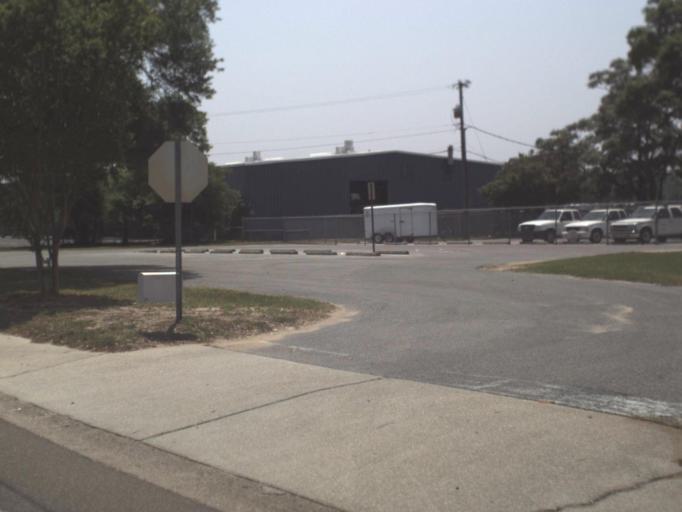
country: US
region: Florida
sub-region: Escambia County
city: Goulding
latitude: 30.4417
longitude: -87.2245
